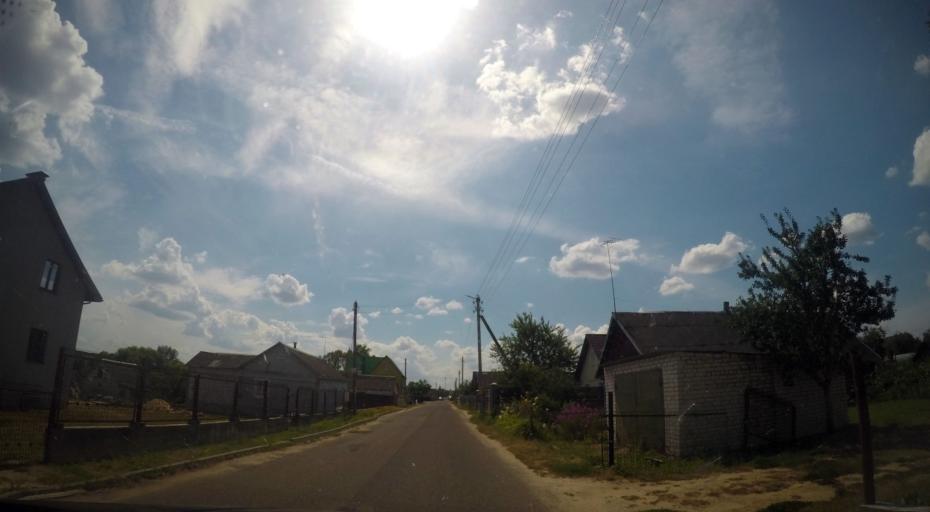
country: BY
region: Grodnenskaya
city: Hrodna
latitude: 53.6289
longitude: 23.8414
